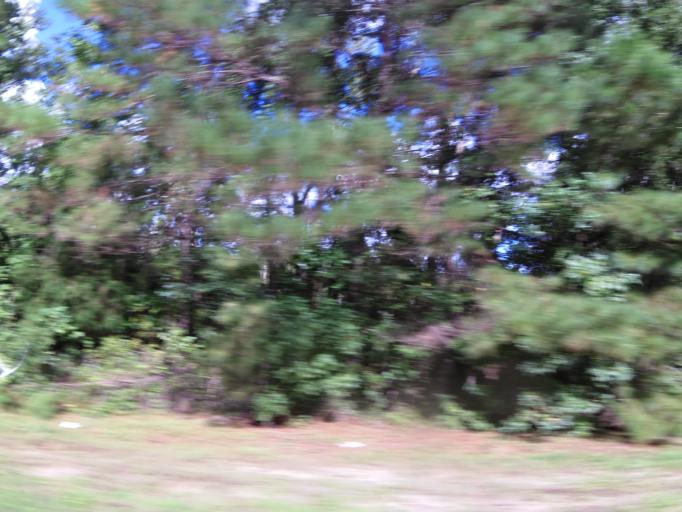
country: US
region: Georgia
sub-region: Camden County
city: Kingsland
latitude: 30.8394
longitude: -81.6981
